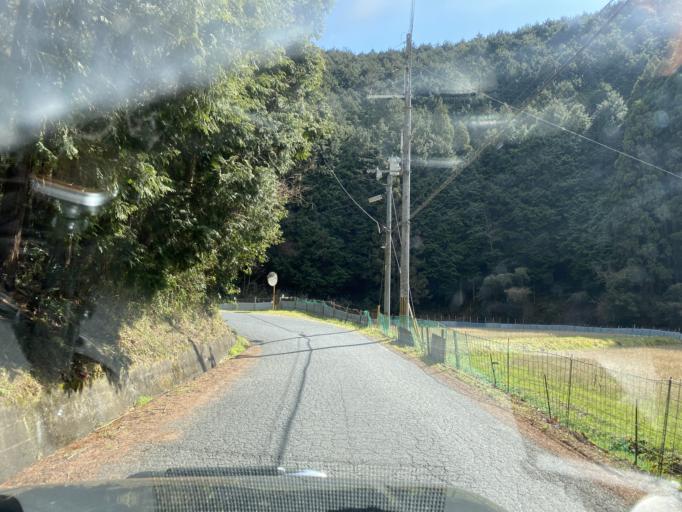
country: JP
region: Nara
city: Nara-shi
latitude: 34.7038
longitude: 135.9499
